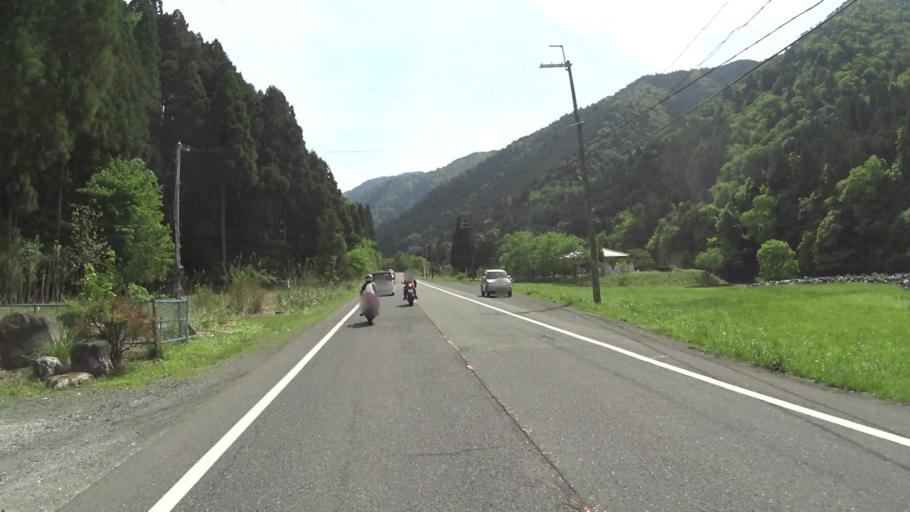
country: JP
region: Shiga Prefecture
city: Kitahama
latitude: 35.3024
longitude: 135.8885
